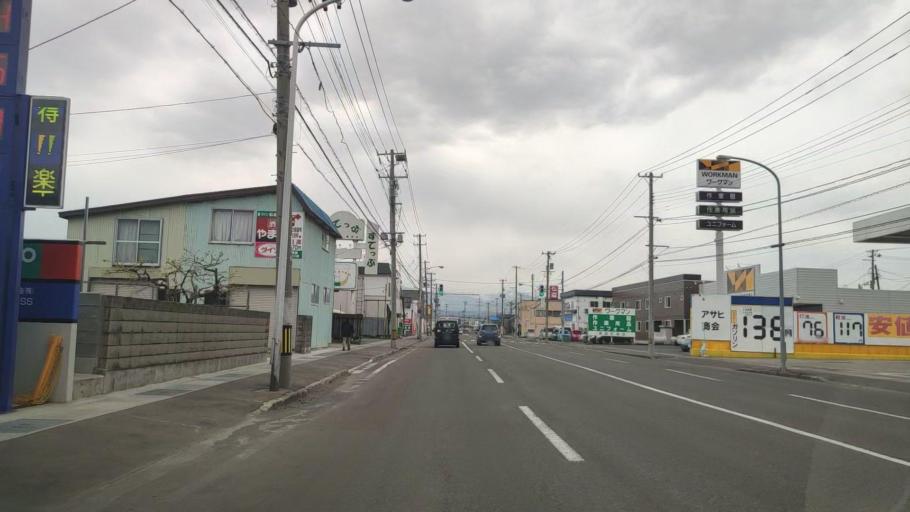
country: JP
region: Aomori
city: Aomori Shi
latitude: 40.8157
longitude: 140.7755
